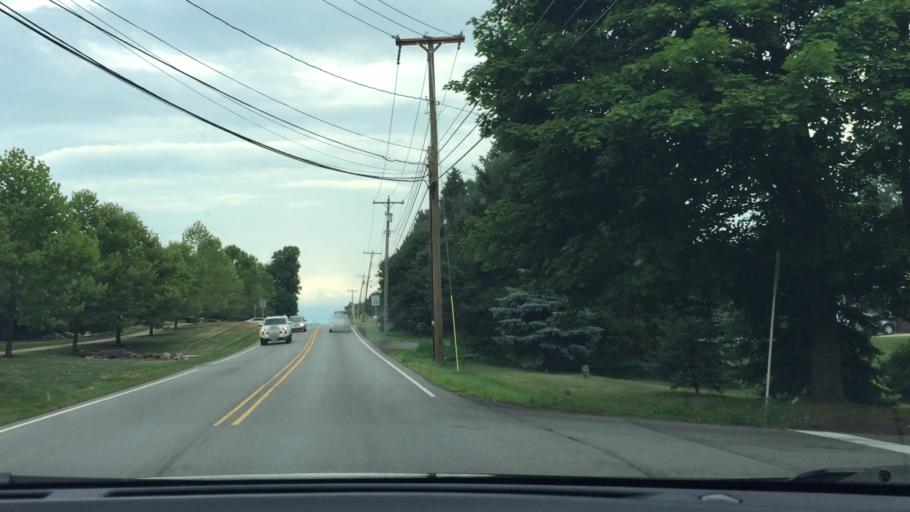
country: US
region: Pennsylvania
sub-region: Butler County
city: Fernway
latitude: 40.6818
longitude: -80.1298
